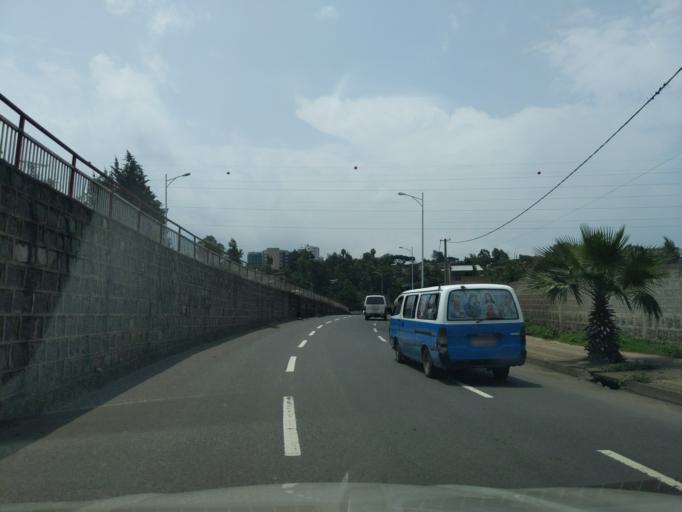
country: ET
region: Adis Abeba
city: Addis Ababa
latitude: 8.9480
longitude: 38.7586
